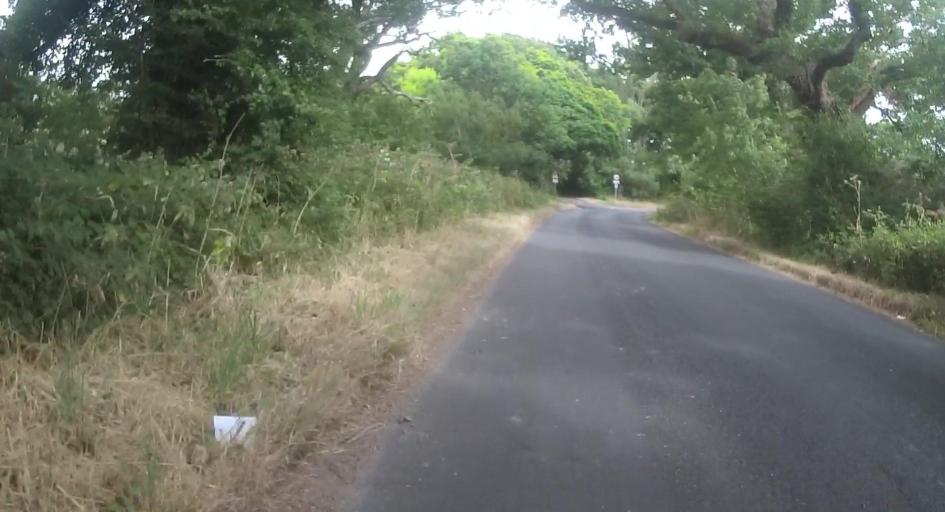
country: GB
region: England
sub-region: Dorset
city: Wool
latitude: 50.6702
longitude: -2.1686
